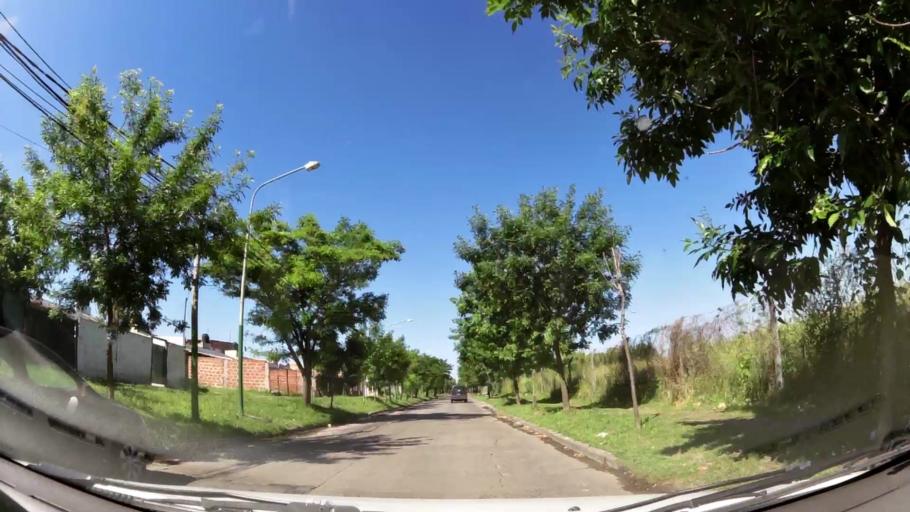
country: AR
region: Buenos Aires
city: Hurlingham
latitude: -34.6183
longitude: -58.6530
